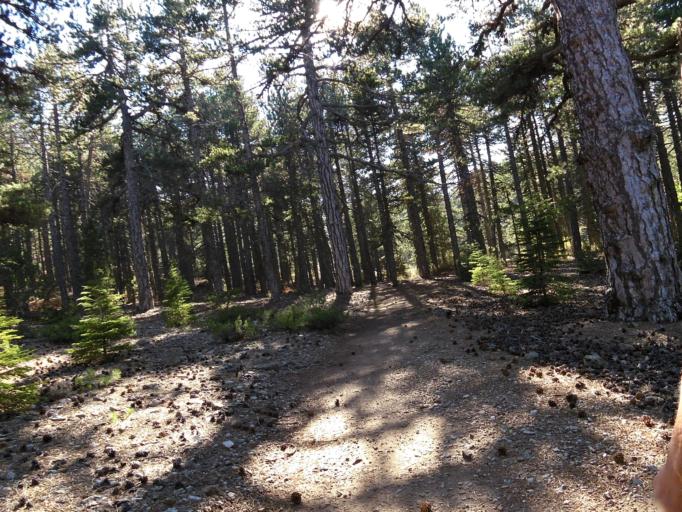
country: CY
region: Lefkosia
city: Kakopetria
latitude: 34.9484
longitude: 32.8478
